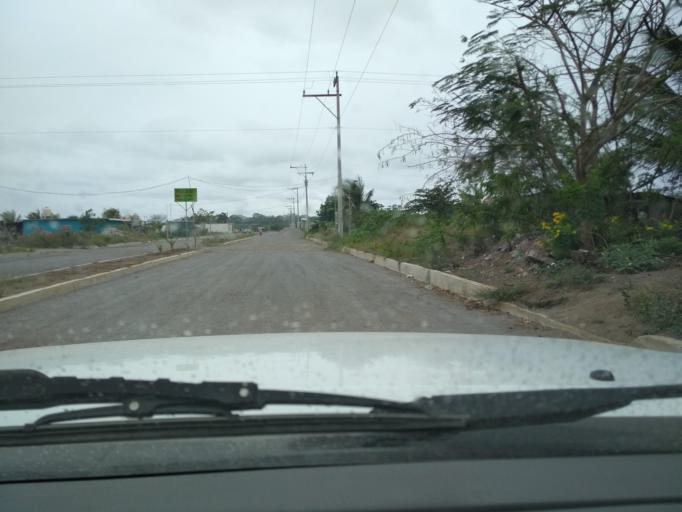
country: MX
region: Veracruz
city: Paso del Toro
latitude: 19.0423
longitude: -96.1316
